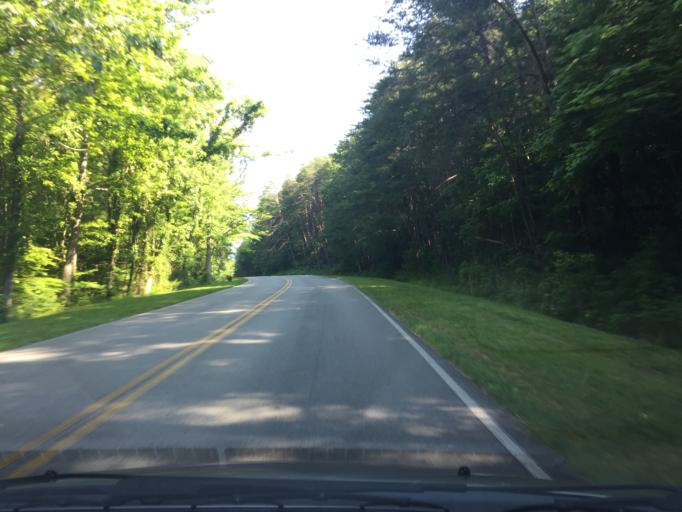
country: US
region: Tennessee
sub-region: Hamilton County
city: Lookout Mountain
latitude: 35.0447
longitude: -85.4244
